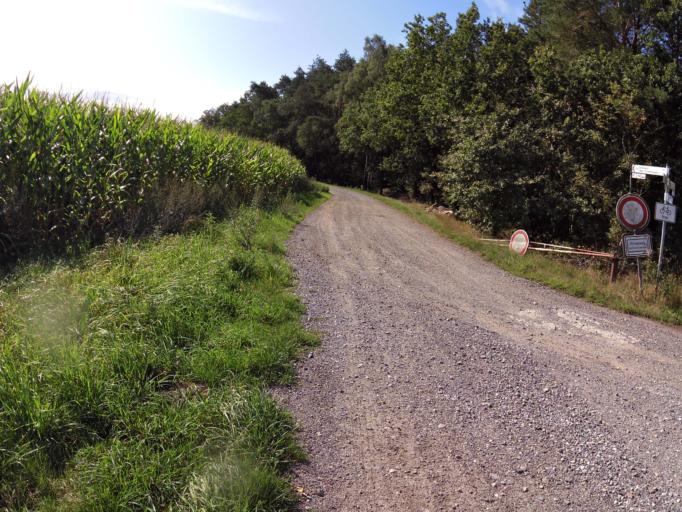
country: DE
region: Lower Saxony
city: Sandbostel
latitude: 53.4017
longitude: 9.1187
